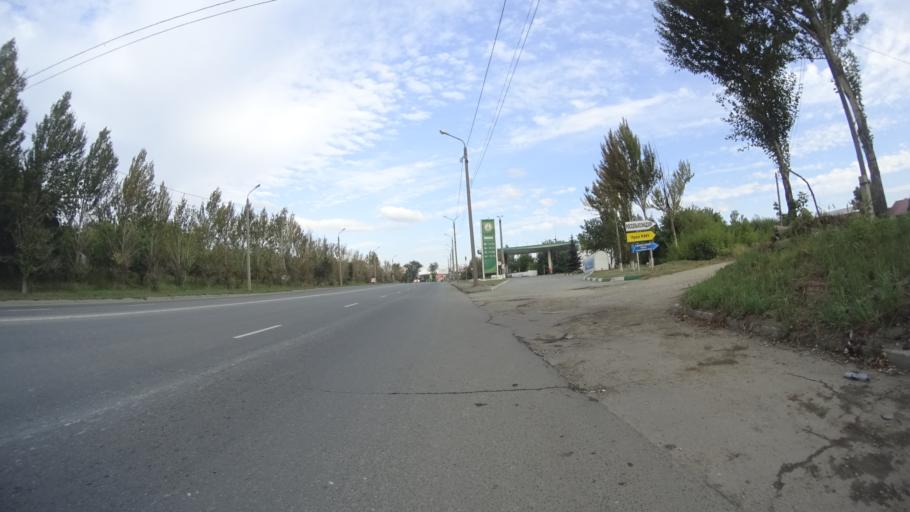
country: RU
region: Chelyabinsk
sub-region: Gorod Chelyabinsk
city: Chelyabinsk
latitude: 55.1928
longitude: 61.4208
